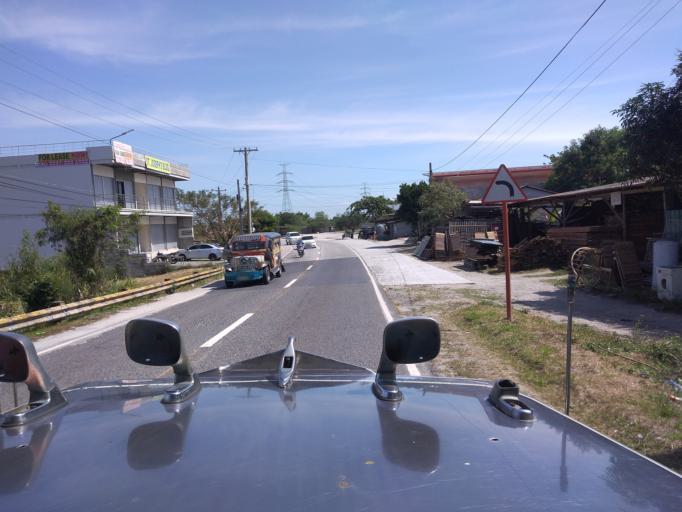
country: PH
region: Central Luzon
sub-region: Province of Pampanga
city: Bacolor
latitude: 15.0077
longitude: 120.6594
